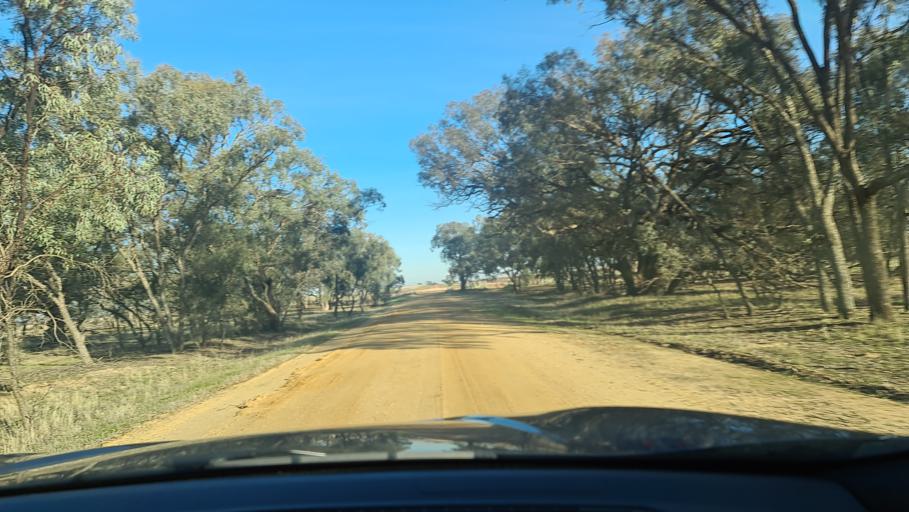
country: AU
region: Victoria
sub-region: Horsham
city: Horsham
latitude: -36.3538
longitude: 142.3972
